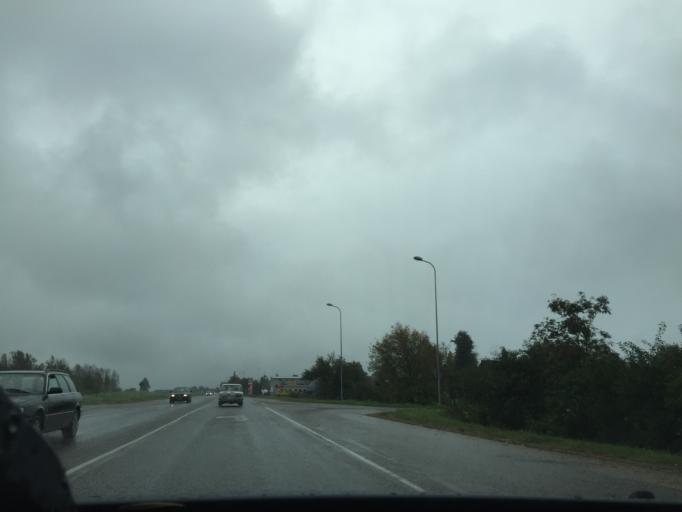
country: LV
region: Jekabpils Rajons
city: Jekabpils
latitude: 56.5119
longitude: 25.8720
